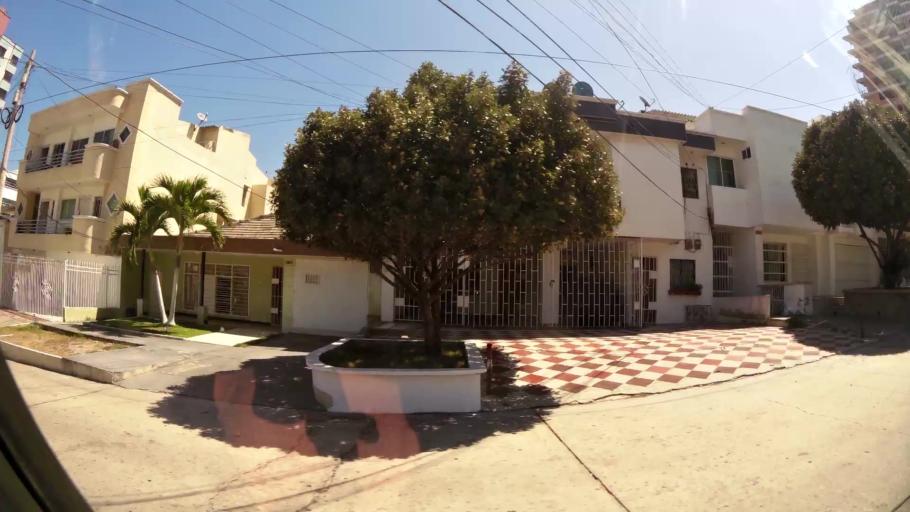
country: CO
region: Atlantico
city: Barranquilla
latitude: 10.9900
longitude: -74.8088
